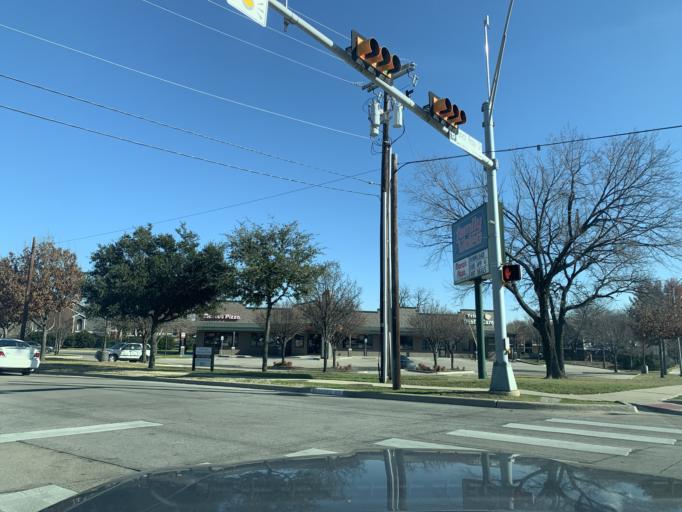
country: US
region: Texas
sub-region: Tarrant County
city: Bedford
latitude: 32.8443
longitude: -97.1432
